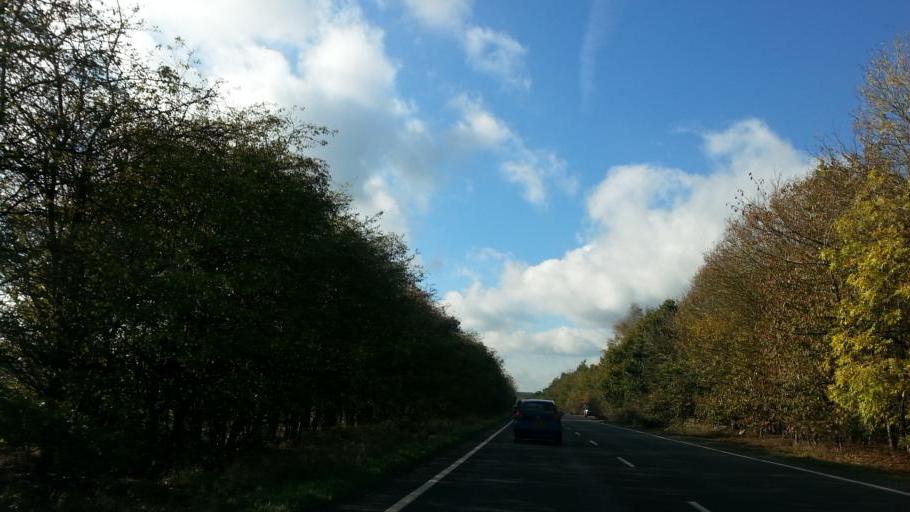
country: GB
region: England
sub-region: Norfolk
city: Loddon
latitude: 52.4852
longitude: 1.5053
